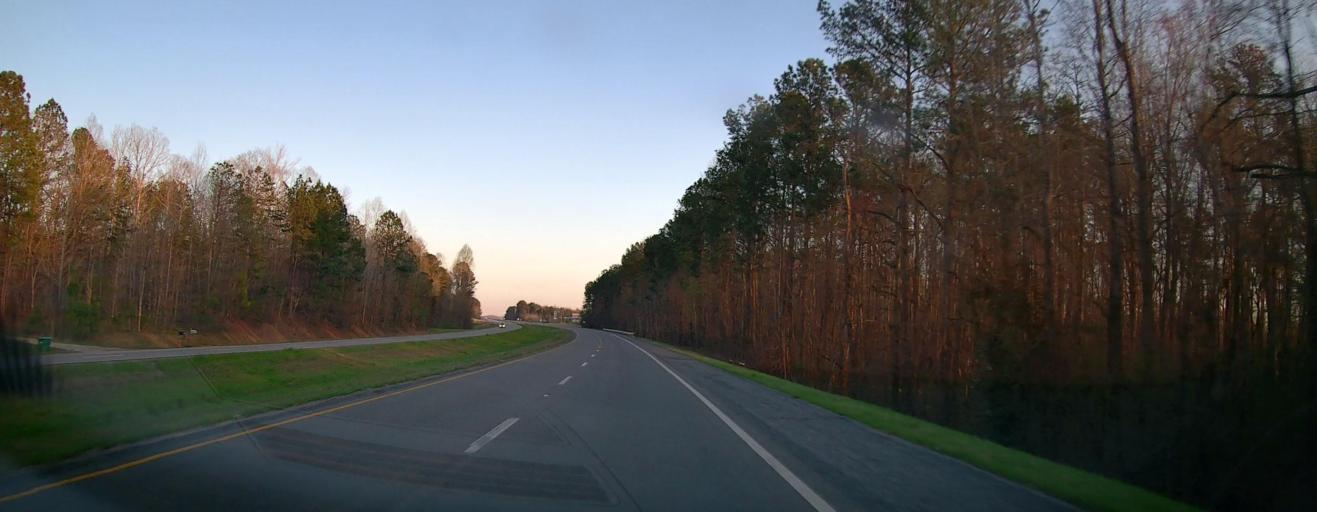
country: US
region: Alabama
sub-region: Coosa County
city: Stewartville
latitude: 33.1155
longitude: -86.2384
